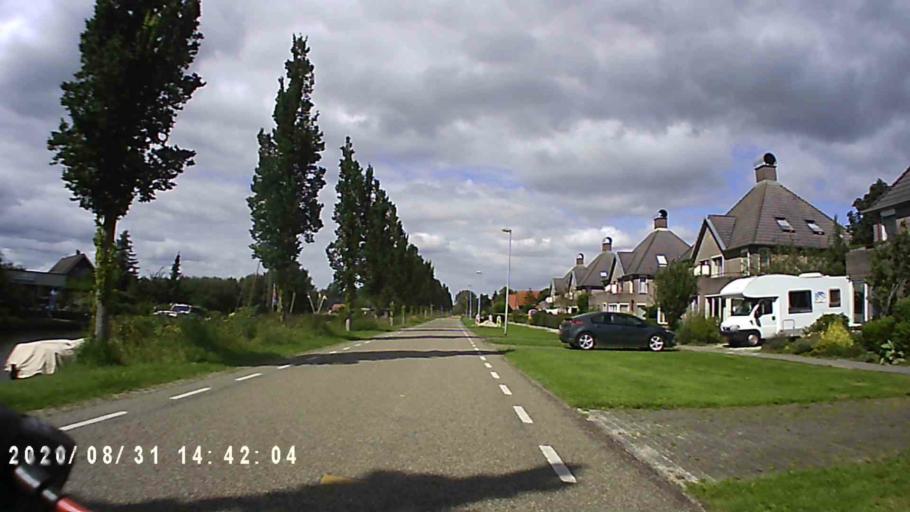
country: NL
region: Groningen
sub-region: Gemeente Zuidhorn
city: Zuidhorn
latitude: 53.2433
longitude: 6.3884
